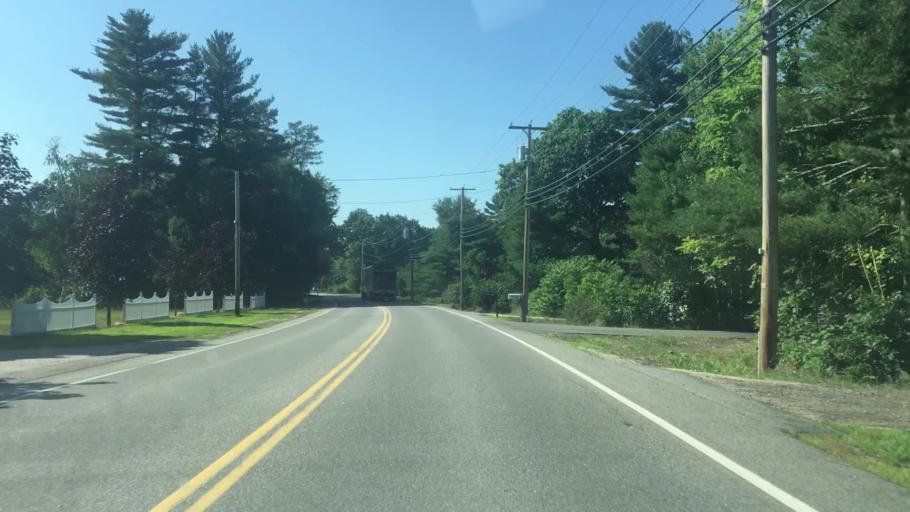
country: US
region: Maine
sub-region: York County
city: Biddeford
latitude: 43.5514
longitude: -70.4919
